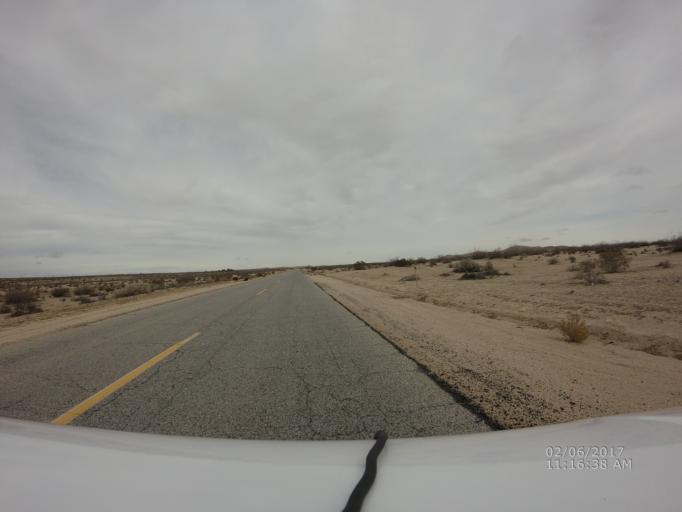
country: US
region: California
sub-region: Los Angeles County
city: Lake Los Angeles
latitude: 34.6773
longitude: -117.7025
